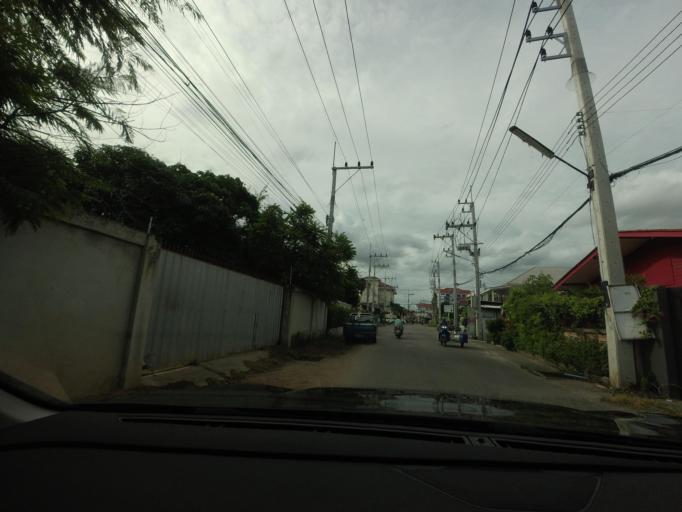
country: TH
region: Prachuap Khiri Khan
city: Hua Hin
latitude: 12.5580
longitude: 99.9550
